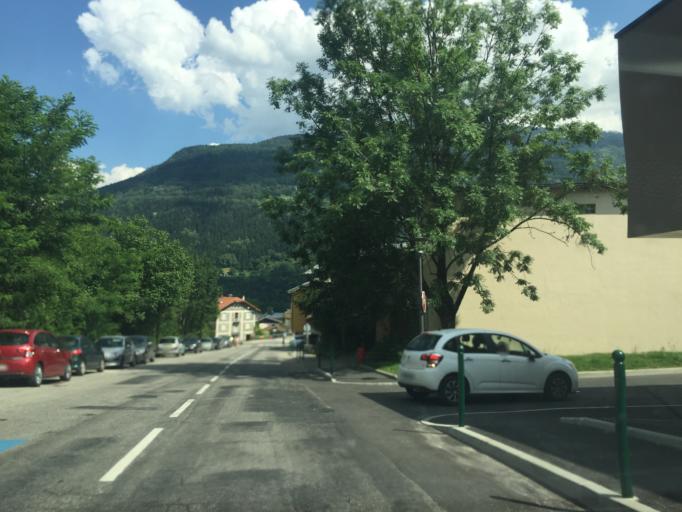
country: FR
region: Rhone-Alpes
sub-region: Departement de la Savoie
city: Bourg-Saint-Maurice
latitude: 45.6166
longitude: 6.7650
